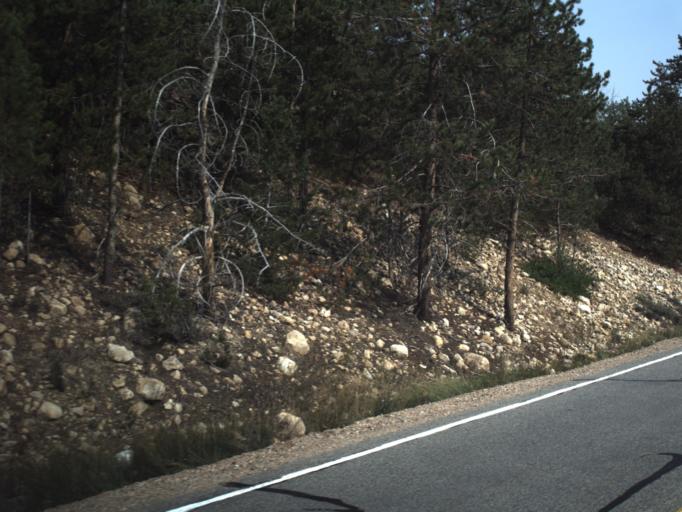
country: US
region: Utah
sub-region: Summit County
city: Francis
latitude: 40.6113
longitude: -111.1250
